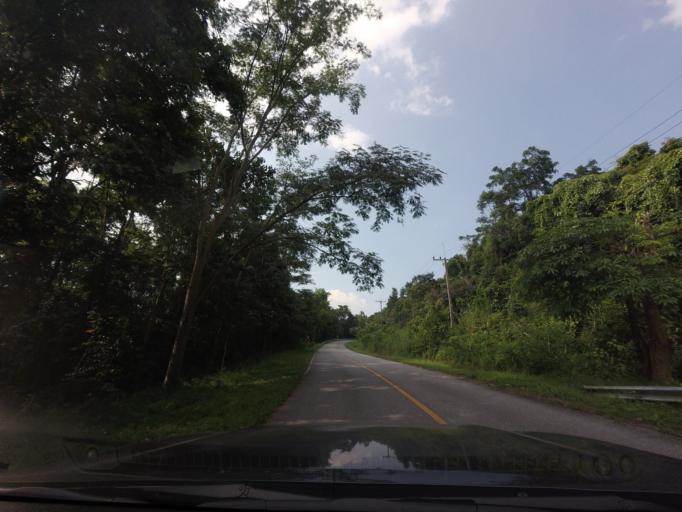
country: TH
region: Phitsanulok
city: Nakhon Thai
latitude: 17.0197
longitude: 100.9639
